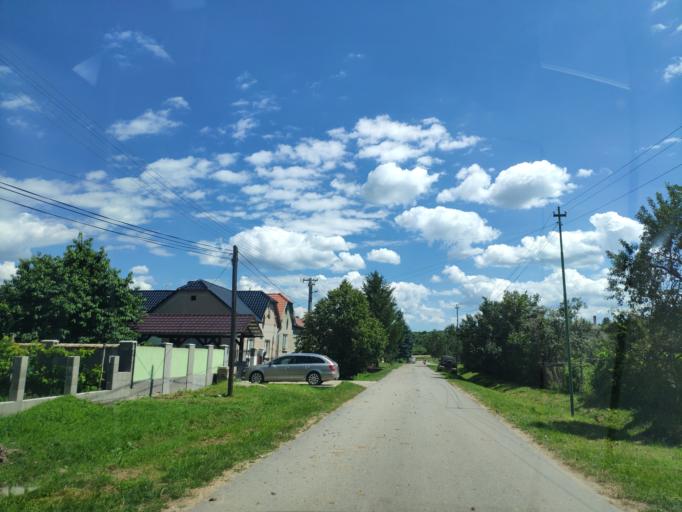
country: HU
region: Borsod-Abauj-Zemplen
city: Arlo
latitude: 48.2805
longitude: 20.1901
